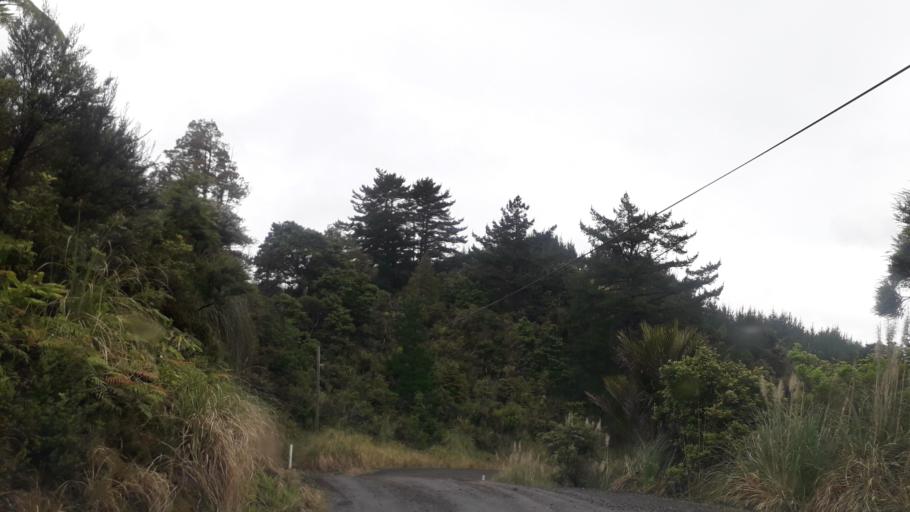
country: NZ
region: Northland
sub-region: Far North District
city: Kaitaia
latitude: -35.3685
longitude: 173.4116
